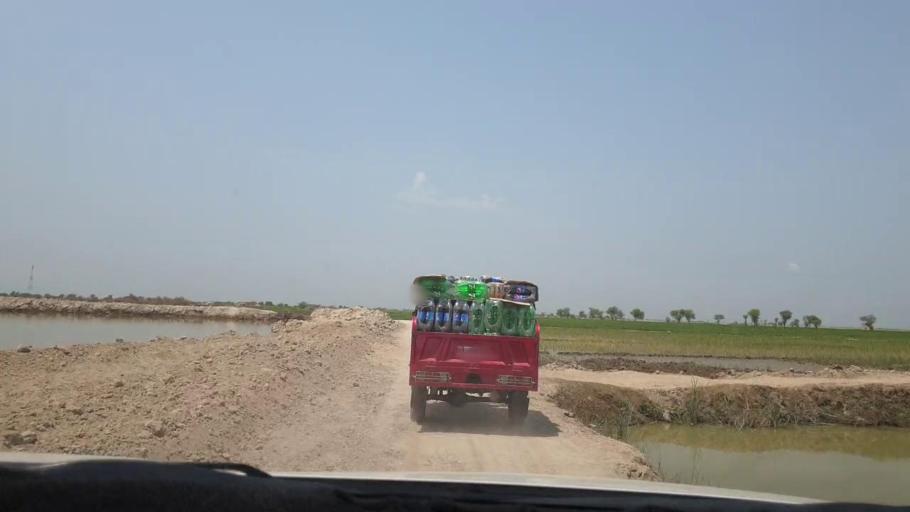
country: PK
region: Sindh
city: Radhan
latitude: 27.2432
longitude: 68.0029
